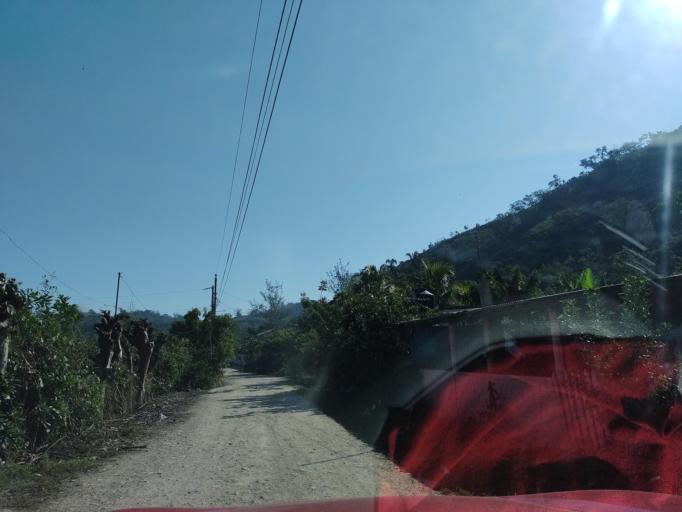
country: MX
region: Veracruz
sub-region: Papantla
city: Polutla
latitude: 20.4965
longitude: -97.1787
